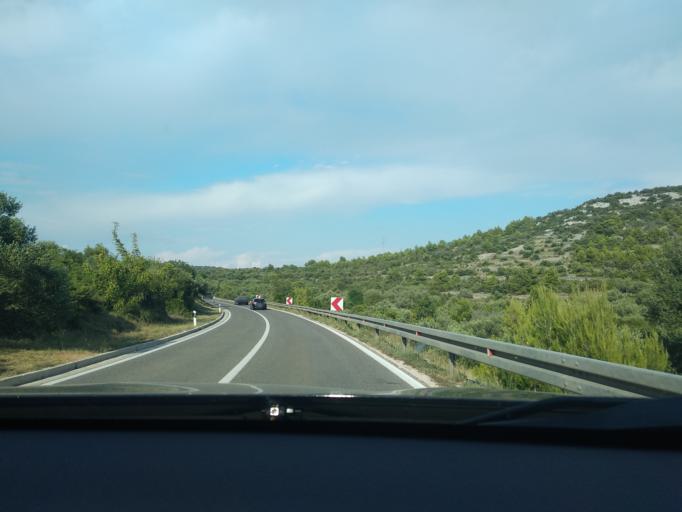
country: HR
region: Sibensko-Kniniska
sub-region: Grad Sibenik
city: Tisno
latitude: 43.8015
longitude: 15.6609
